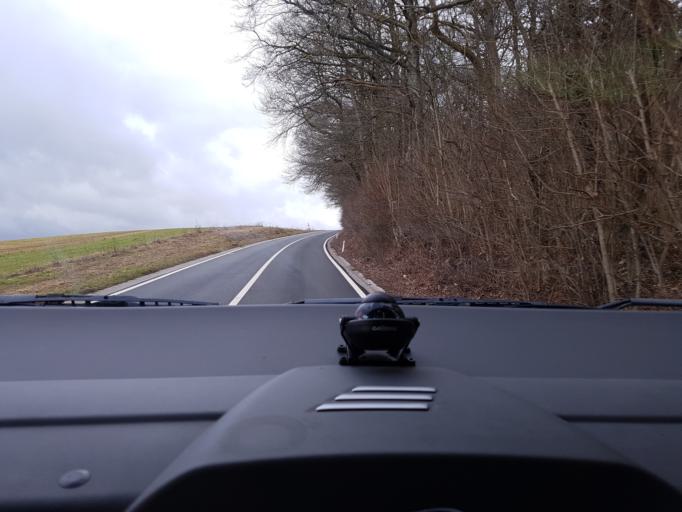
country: BE
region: Wallonia
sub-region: Province de Namur
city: Ciney
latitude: 50.2832
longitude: 5.1462
